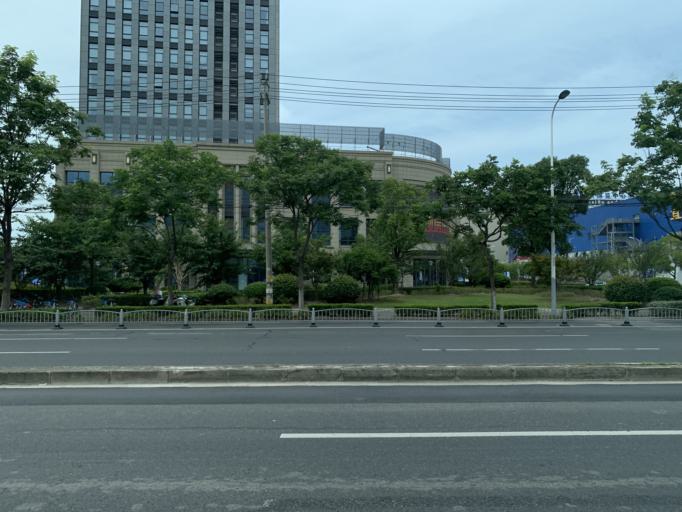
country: CN
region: Shanghai Shi
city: Kangqiao
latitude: 31.1607
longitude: 121.5598
